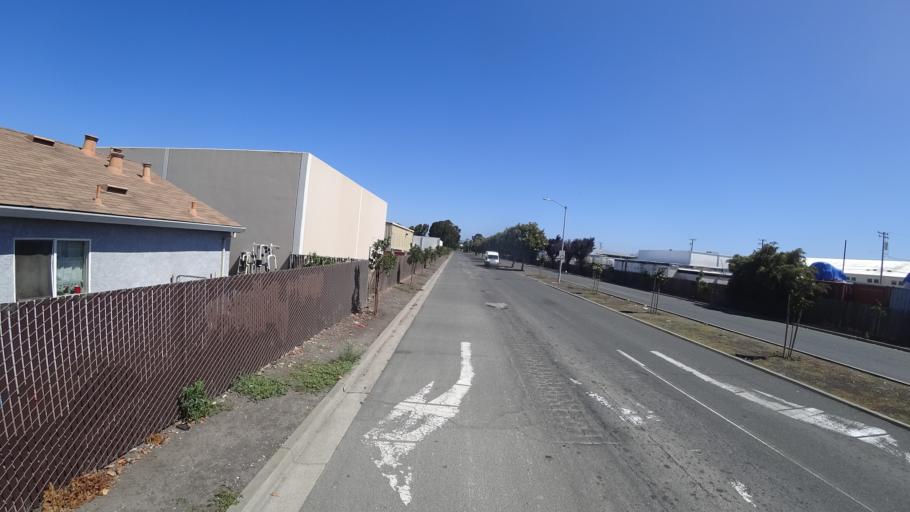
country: US
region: California
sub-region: Alameda County
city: San Lorenzo
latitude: 37.6534
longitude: -122.1248
